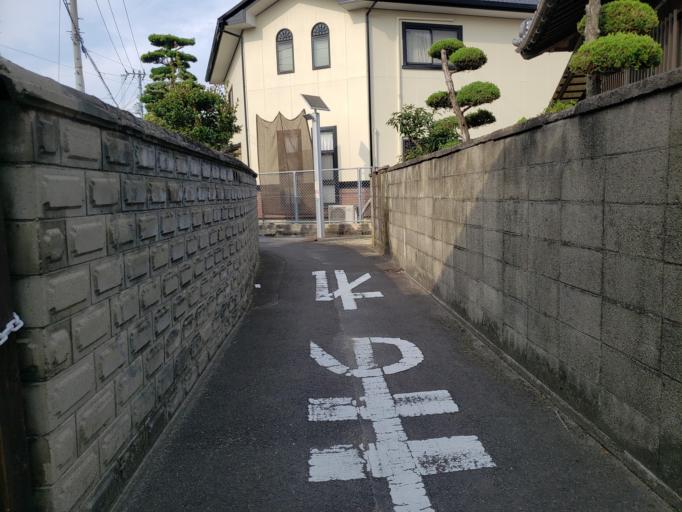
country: JP
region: Kagawa
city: Marugame
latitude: 34.2340
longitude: 133.7890
